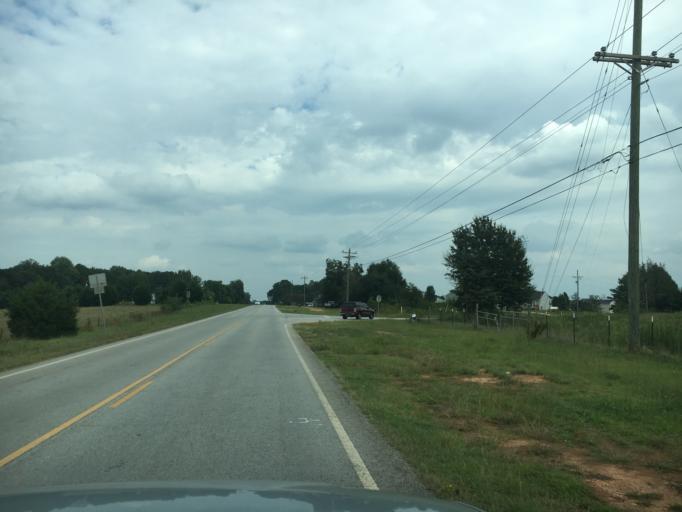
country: US
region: Georgia
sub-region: Franklin County
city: Gumlog
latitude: 34.4609
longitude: -83.0805
